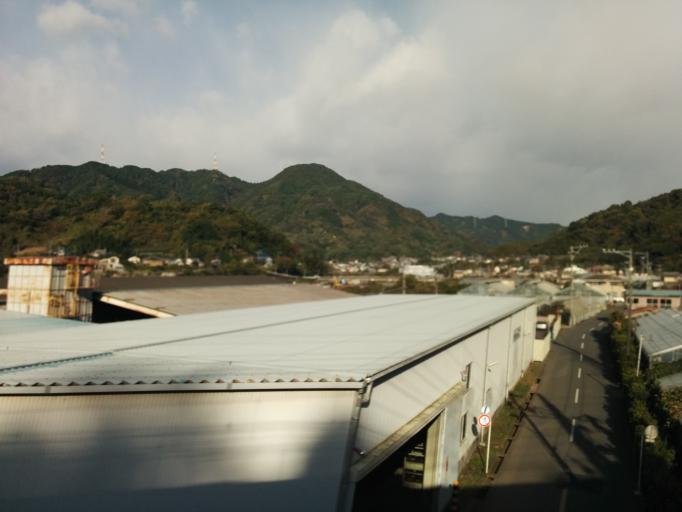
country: JP
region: Shizuoka
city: Fujinomiya
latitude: 35.0759
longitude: 138.5249
